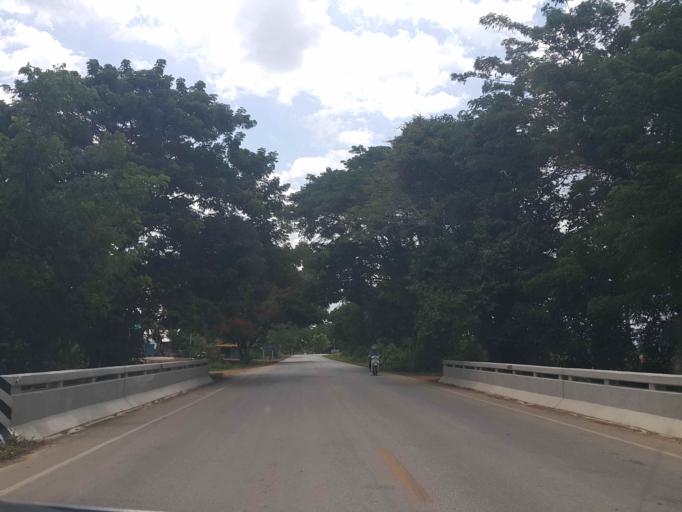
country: TH
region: Sukhothai
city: Thung Saliam
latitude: 17.3296
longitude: 99.6244
